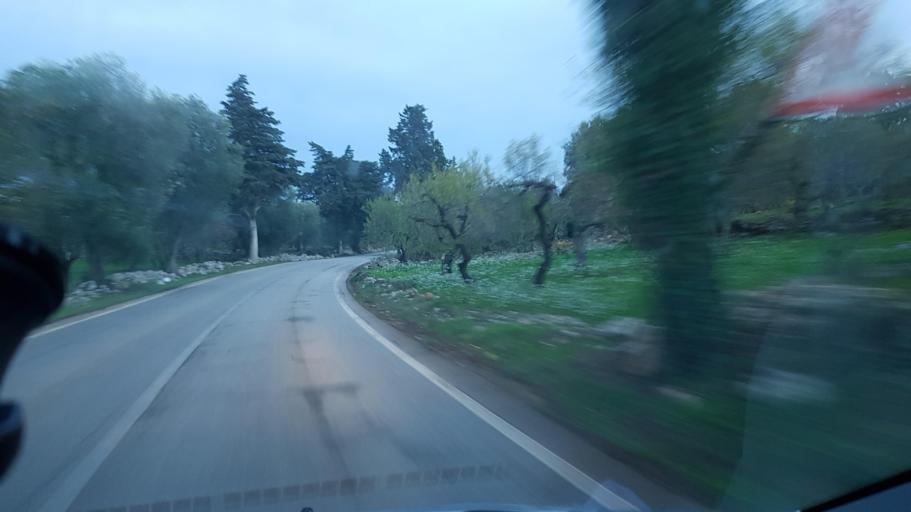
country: IT
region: Apulia
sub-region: Provincia di Brindisi
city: San Michele Salentino
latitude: 40.6428
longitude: 17.5755
